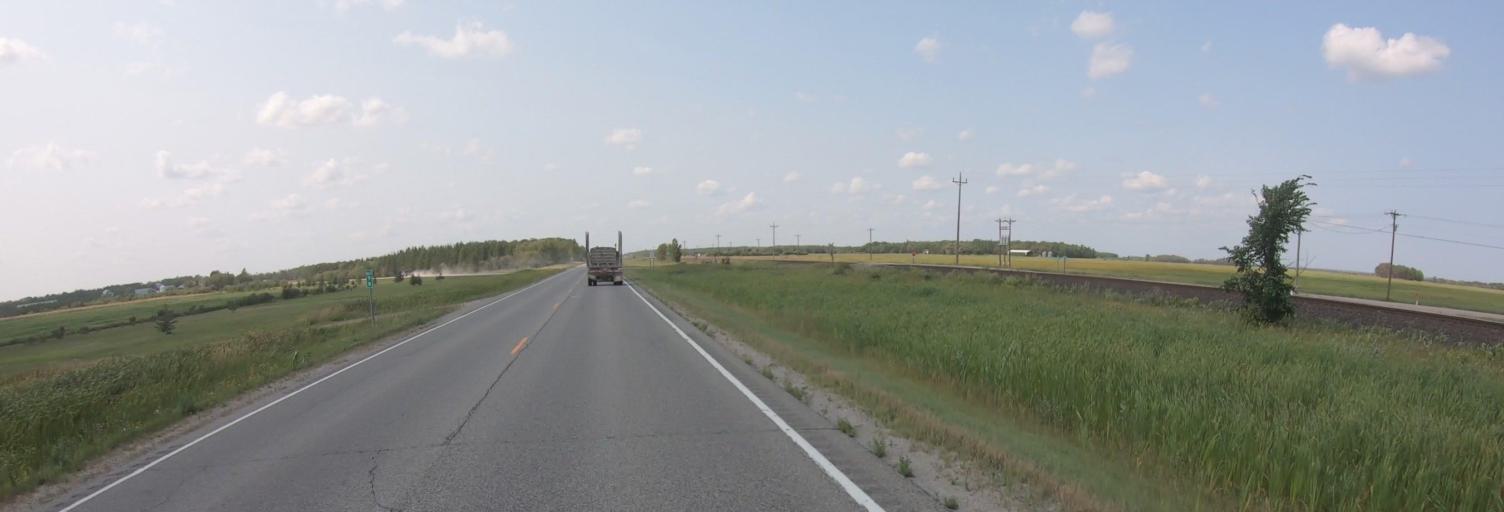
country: US
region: Minnesota
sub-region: Roseau County
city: Warroad
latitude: 48.8571
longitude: -95.2313
